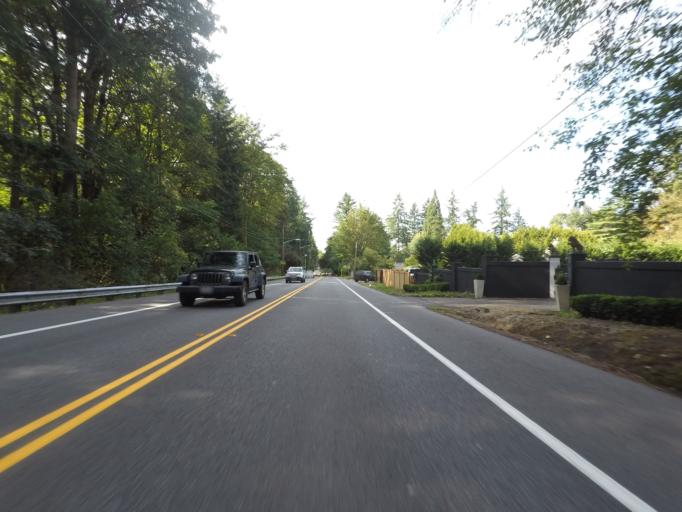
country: US
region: Washington
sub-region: King County
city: Inglewood-Finn Hill
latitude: 47.7347
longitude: -122.2475
